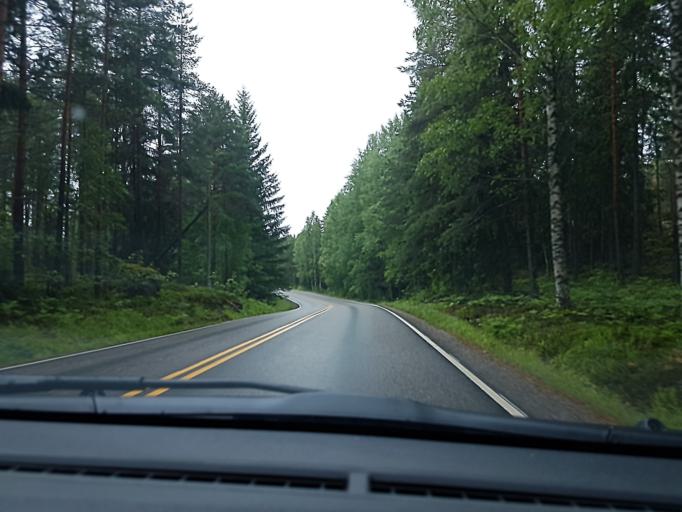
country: FI
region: Uusimaa
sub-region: Helsinki
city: Pornainen
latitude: 60.4589
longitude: 25.3871
